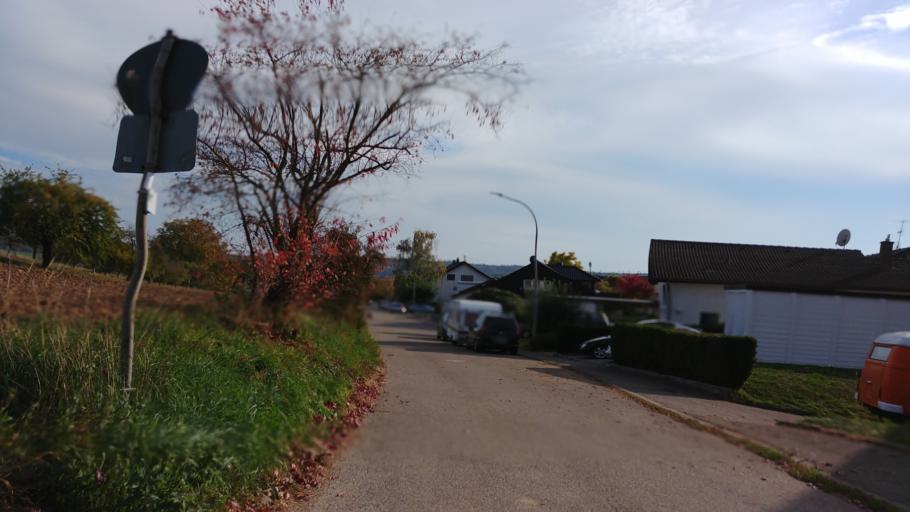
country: DE
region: Baden-Wuerttemberg
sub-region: Regierungsbezirk Stuttgart
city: Ilsfeld
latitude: 49.0609
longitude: 9.2486
